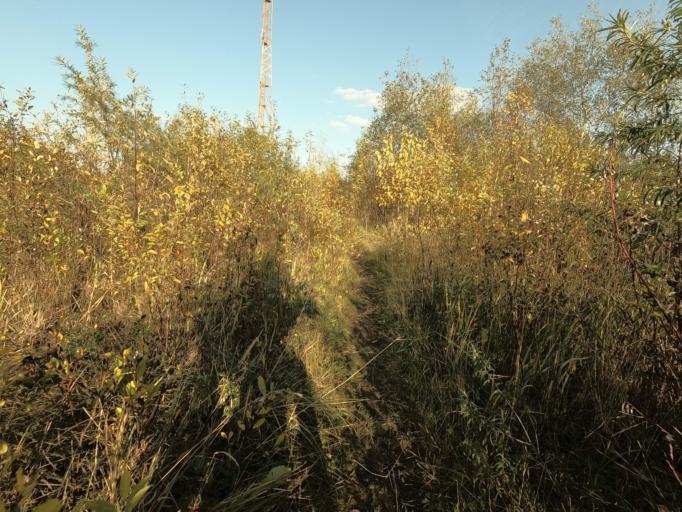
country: RU
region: Leningrad
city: Mga
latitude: 59.7456
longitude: 31.0611
